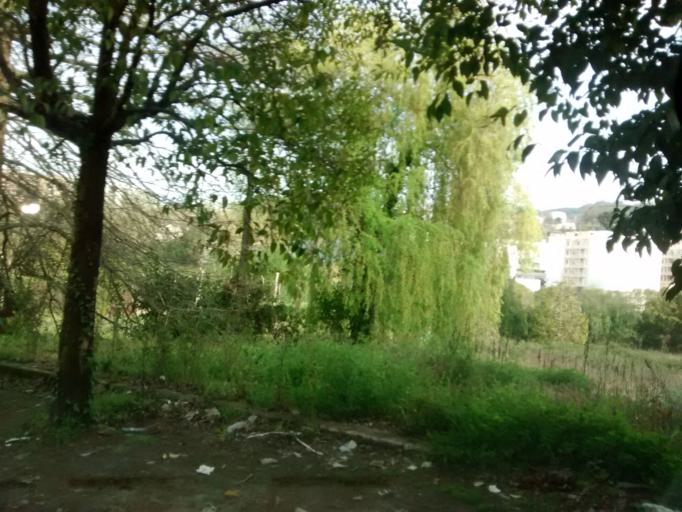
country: PT
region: Braga
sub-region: Guimaraes
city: Guimaraes
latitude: 41.4546
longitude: -8.2878
